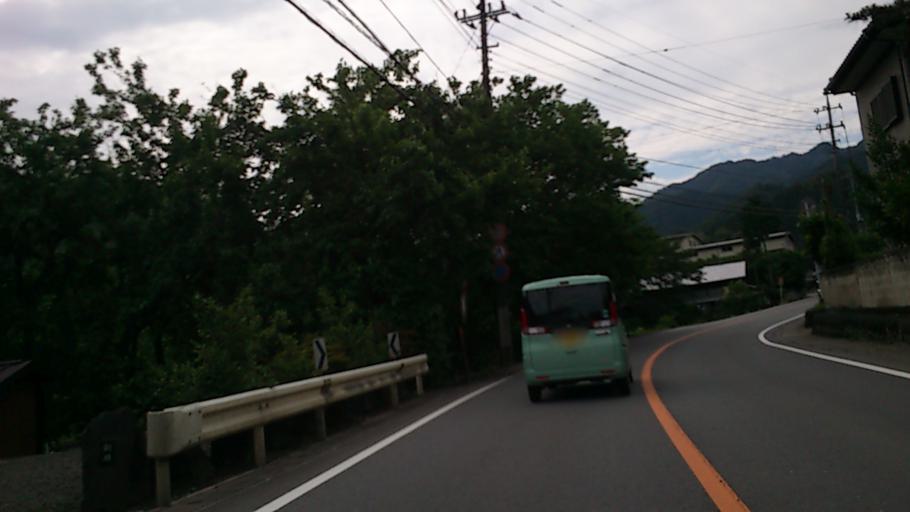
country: JP
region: Gunma
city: Tomioka
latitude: 36.2276
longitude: 138.7638
